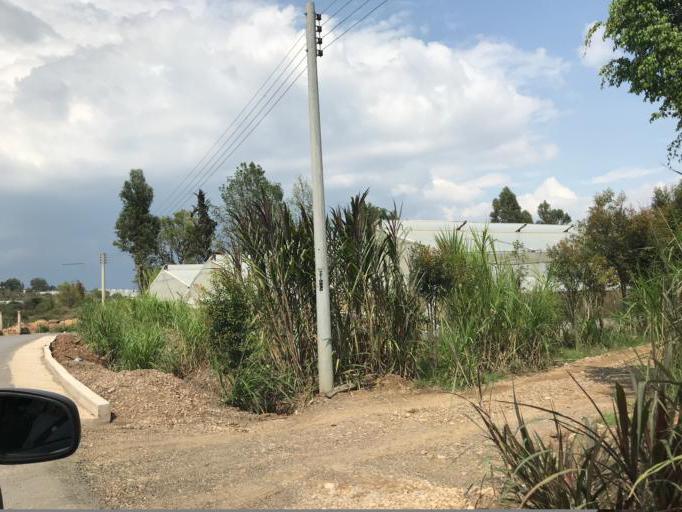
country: CO
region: Boyaca
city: Sutamarchan
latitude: 5.6286
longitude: -73.6119
